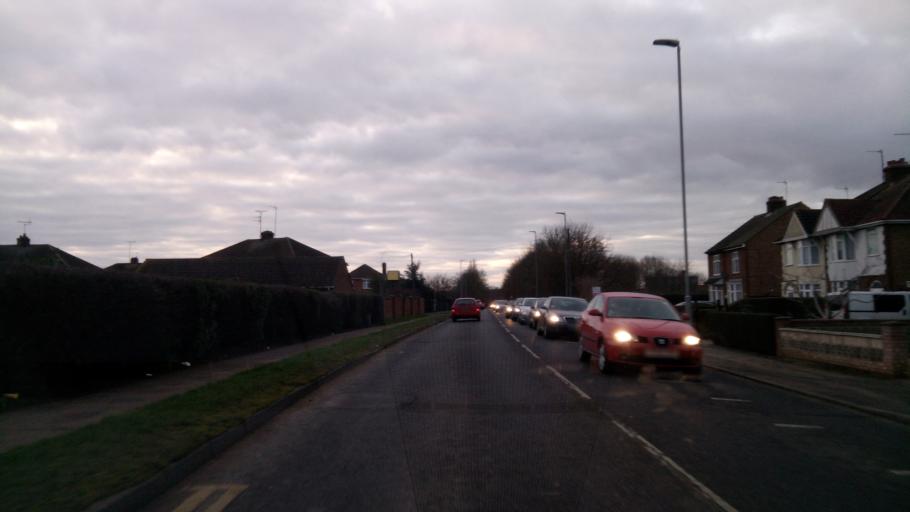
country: GB
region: England
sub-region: Peterborough
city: Peterborough
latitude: 52.5507
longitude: -0.2198
